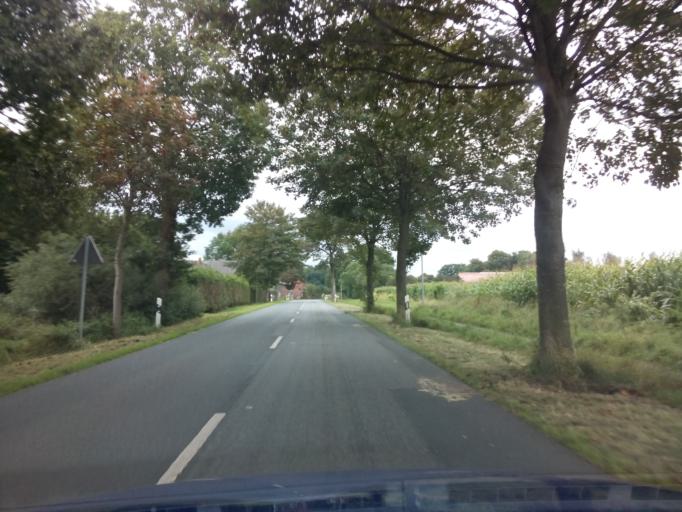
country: DE
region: Lower Saxony
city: Beverstedt
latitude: 53.4481
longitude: 8.8318
